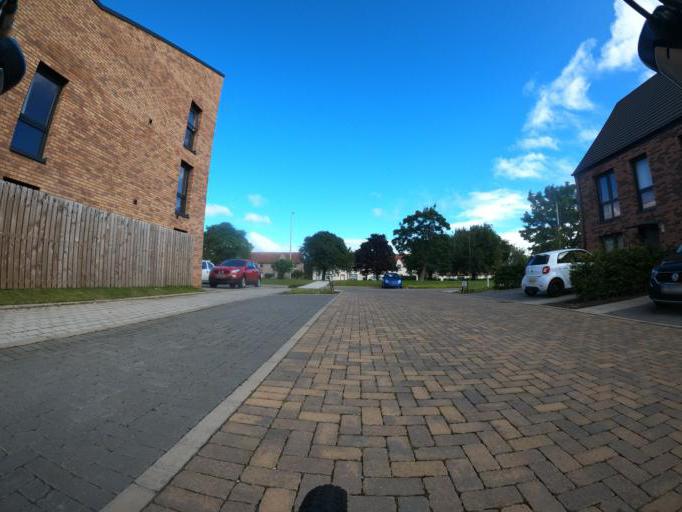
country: GB
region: Scotland
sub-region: Edinburgh
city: Edinburgh
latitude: 55.9742
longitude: -3.2559
